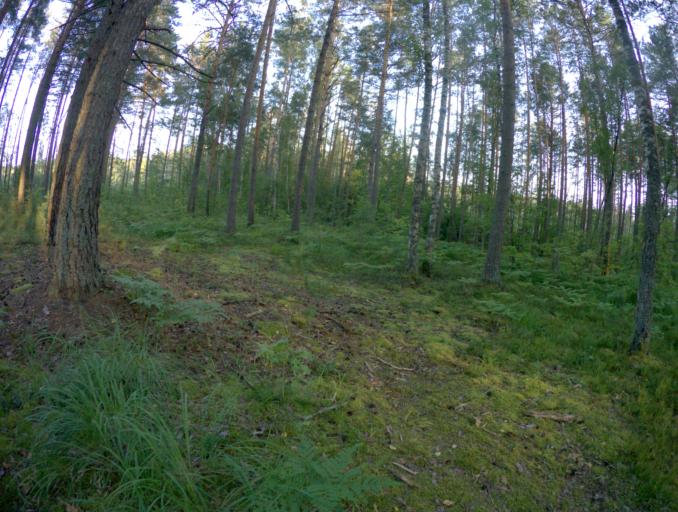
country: RU
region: Vladimir
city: Kommunar
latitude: 56.0931
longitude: 40.4603
